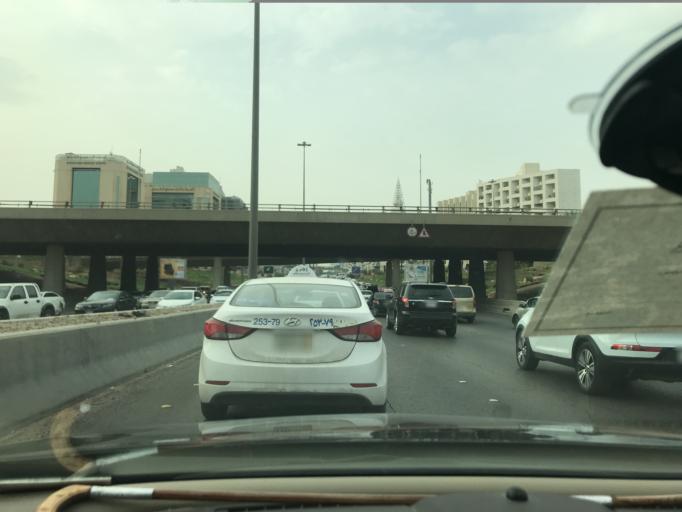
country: SA
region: Ar Riyad
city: Riyadh
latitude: 24.6781
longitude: 46.6892
